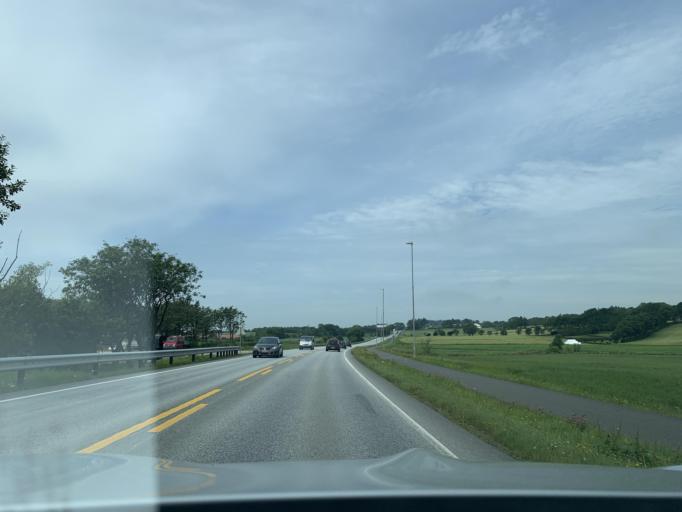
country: NO
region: Rogaland
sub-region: Time
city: Bryne
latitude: 58.7476
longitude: 5.6313
